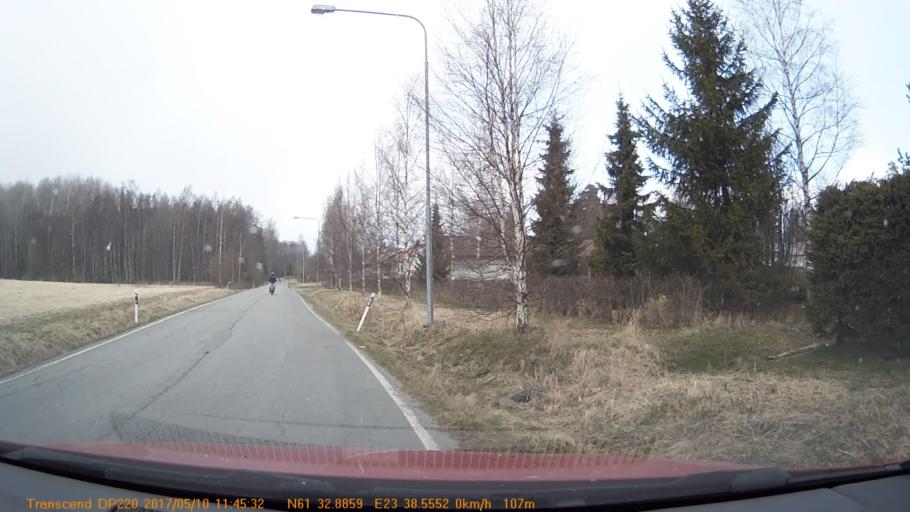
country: FI
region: Pirkanmaa
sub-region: Tampere
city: Yloejaervi
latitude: 61.5482
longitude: 23.6426
